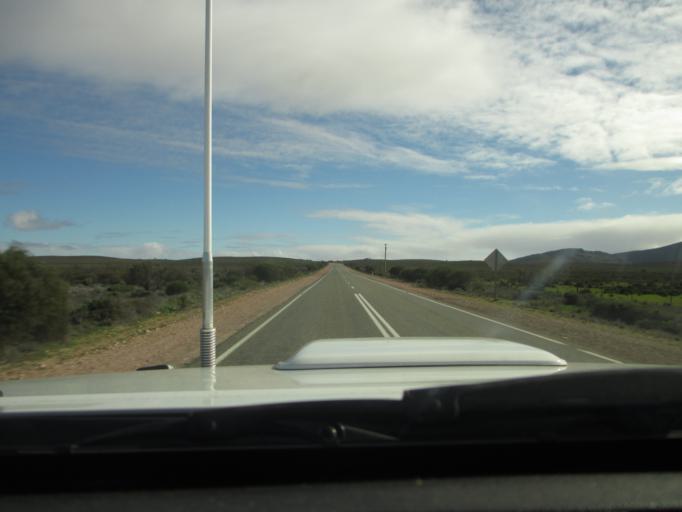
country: AU
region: South Australia
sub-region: Flinders Ranges
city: Quorn
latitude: -31.8186
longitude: 138.3760
